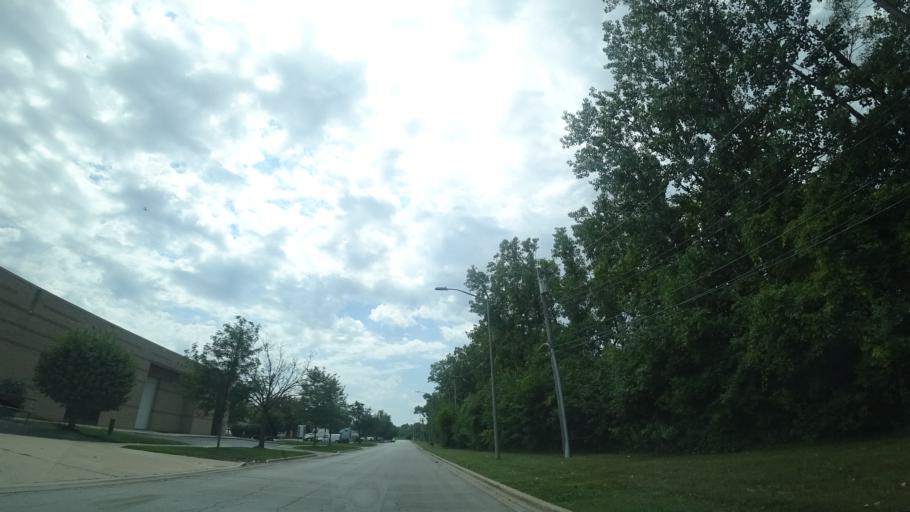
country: US
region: Illinois
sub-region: Cook County
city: Crestwood
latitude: 41.6646
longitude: -87.7486
